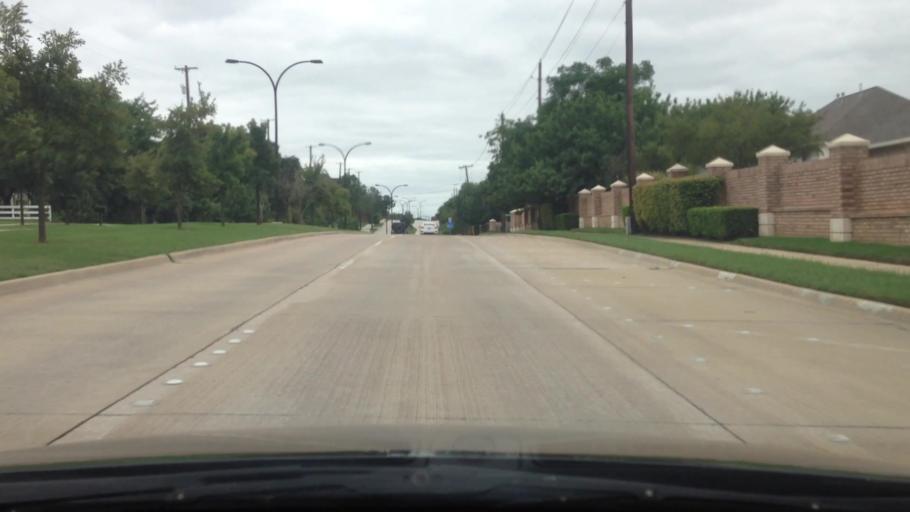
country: US
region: Texas
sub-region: Tarrant County
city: Keller
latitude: 32.9202
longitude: -97.2322
